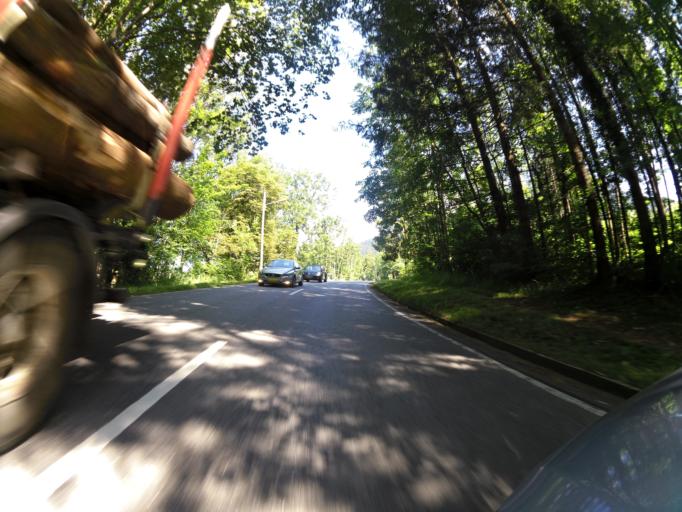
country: DE
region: Bavaria
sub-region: Upper Bavaria
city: Berchtesgaden
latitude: 47.6325
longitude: 13.0135
